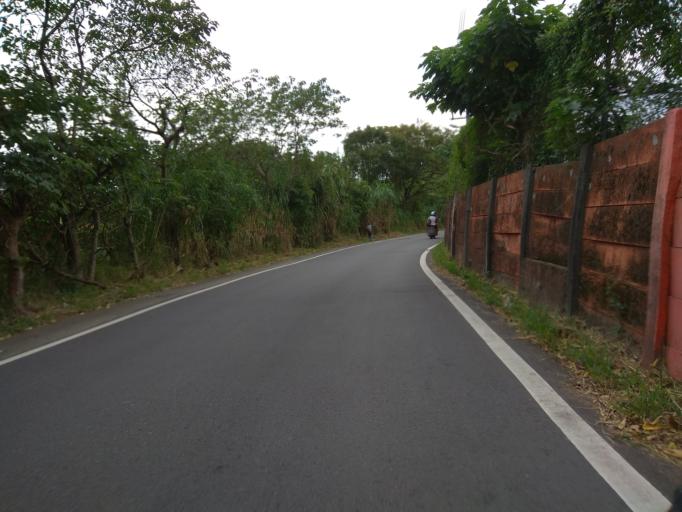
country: TW
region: Taiwan
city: Daxi
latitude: 24.9345
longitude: 121.2050
